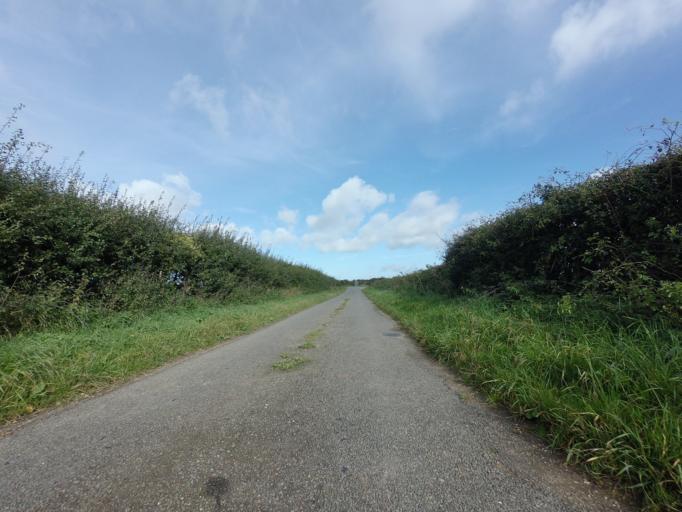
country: GB
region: England
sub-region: Norfolk
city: Wells-next-the-Sea
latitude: 52.9258
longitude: 0.7230
